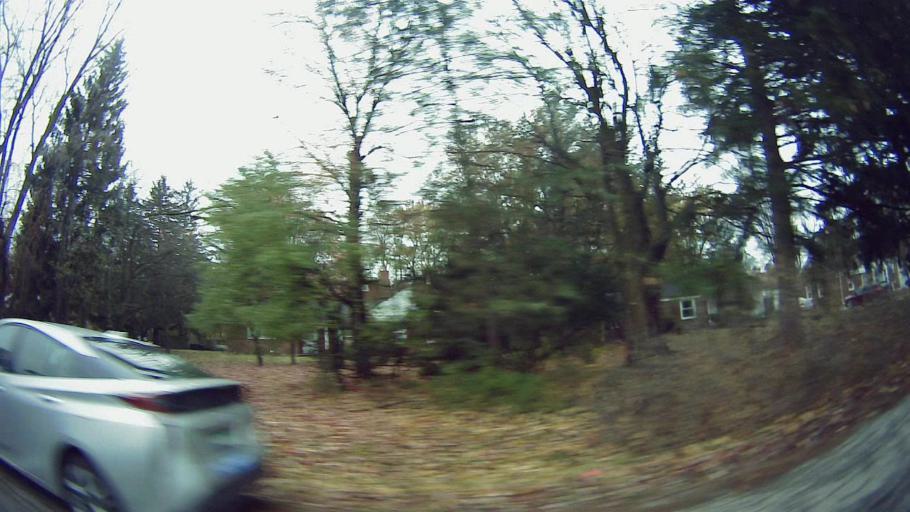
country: US
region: Michigan
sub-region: Oakland County
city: Southfield
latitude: 42.4641
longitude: -83.2368
